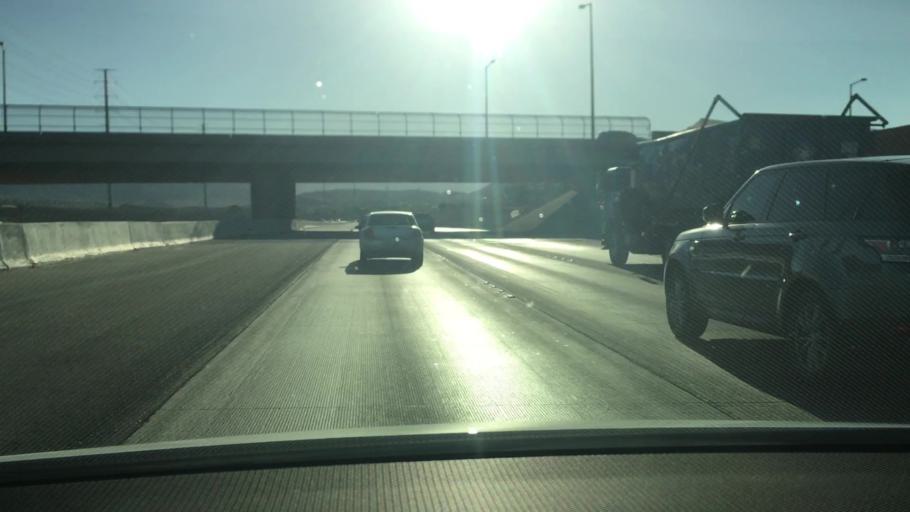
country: US
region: Nevada
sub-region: Clark County
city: Summerlin South
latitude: 36.1189
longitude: -115.3141
